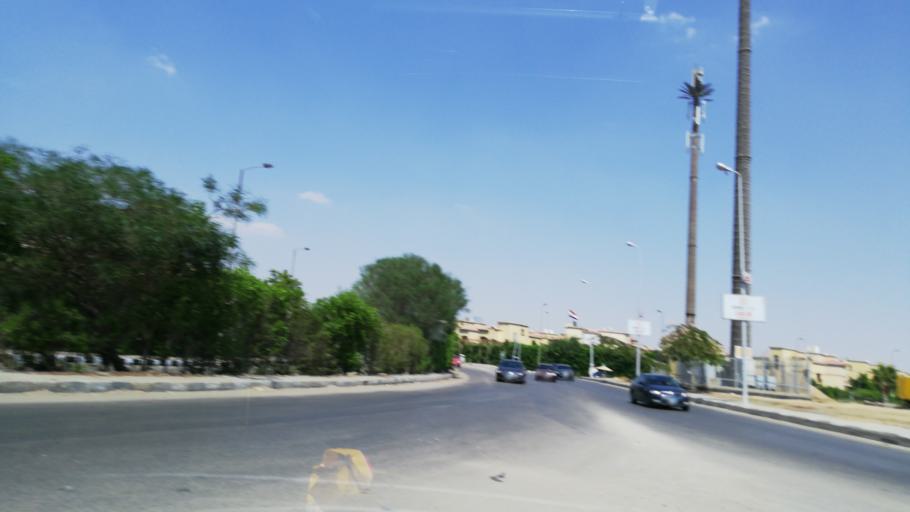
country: EG
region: Muhafazat al Qalyubiyah
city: Al Khankah
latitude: 30.0533
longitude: 31.4983
